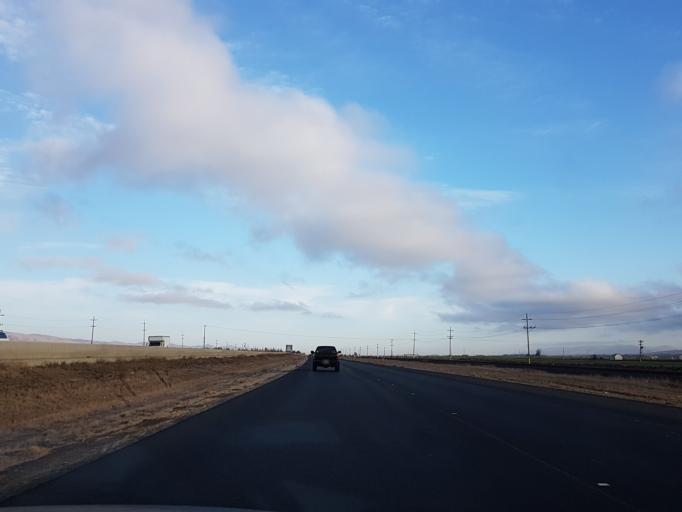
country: US
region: California
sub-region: Monterey County
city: Gonzales
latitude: 36.4824
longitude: -121.4158
